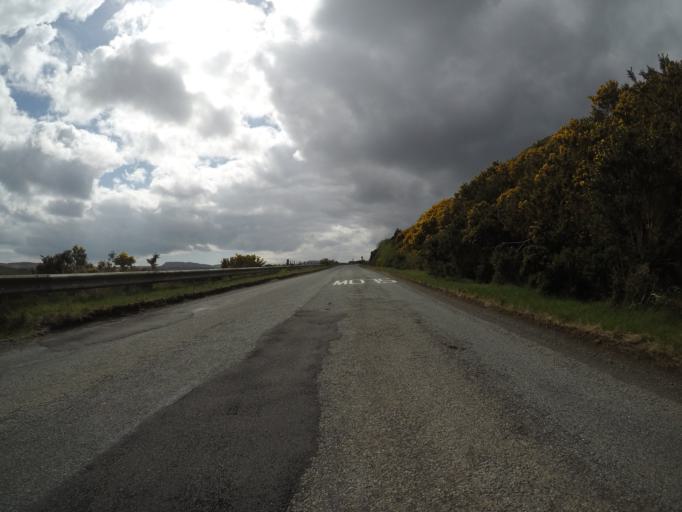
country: GB
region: Scotland
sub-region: Highland
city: Isle of Skye
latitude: 57.3048
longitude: -6.3012
